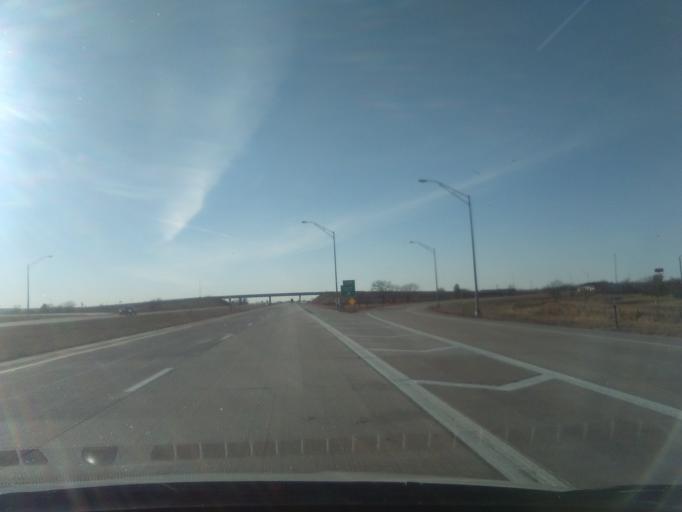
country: US
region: Colorado
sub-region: Sedgwick County
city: Julesburg
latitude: 41.0503
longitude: -102.0662
